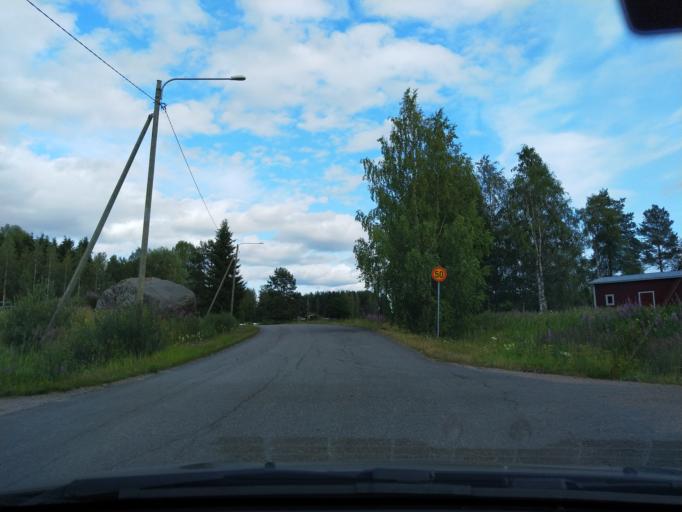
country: FI
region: Kymenlaakso
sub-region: Kouvola
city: Kouvola
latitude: 61.0448
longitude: 26.8307
